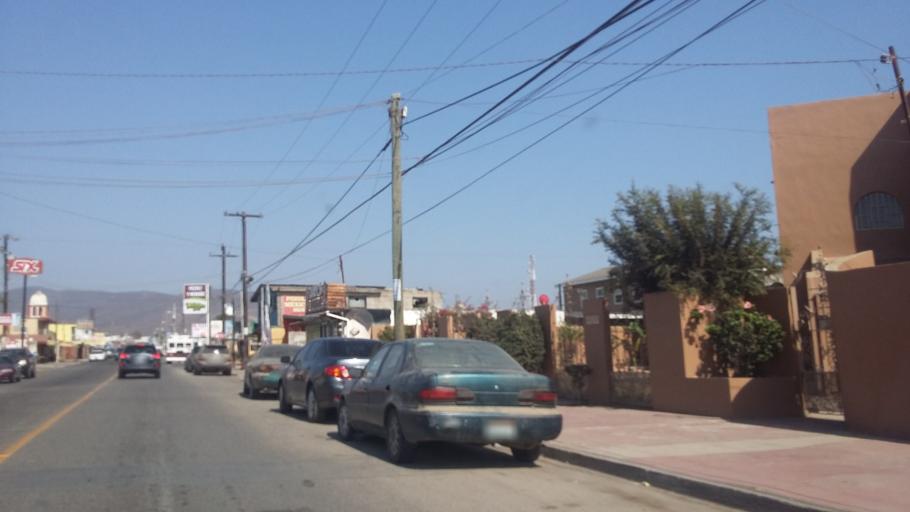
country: MX
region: Baja California
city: Rodolfo Sanchez Taboada
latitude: 31.7835
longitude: -116.5970
